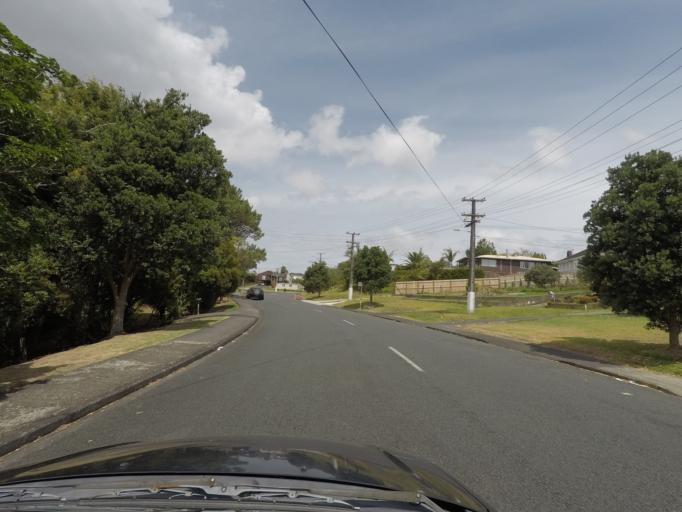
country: NZ
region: Auckland
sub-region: Auckland
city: Waitakere
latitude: -36.8979
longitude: 174.6375
